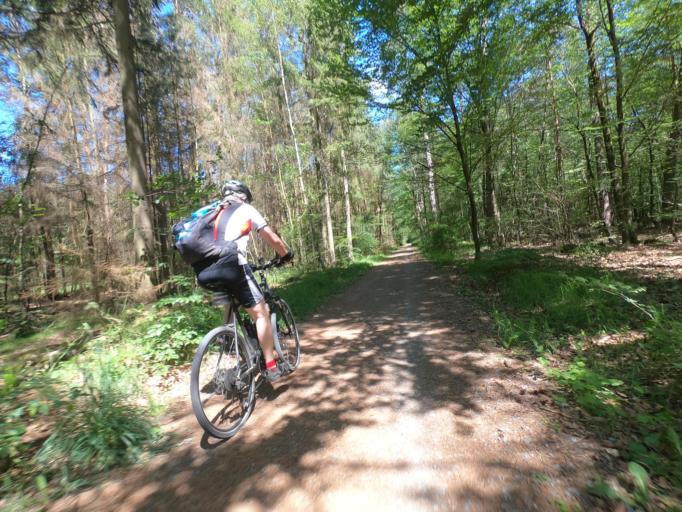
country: DE
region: Hesse
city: Heusenstamm
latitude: 50.0507
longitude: 8.7743
